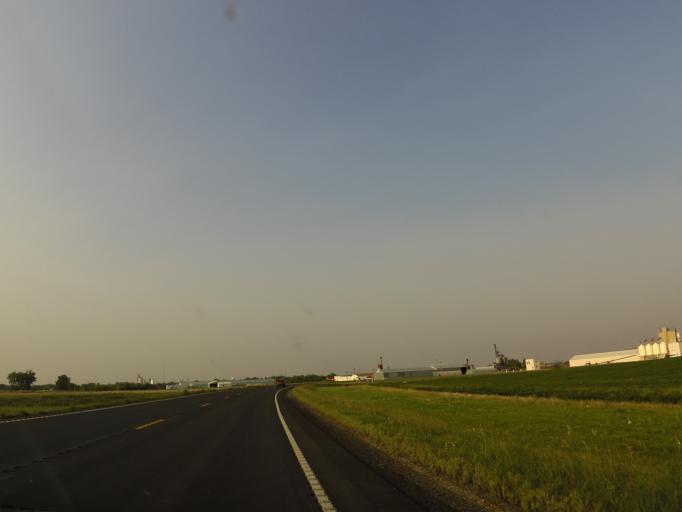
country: US
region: North Dakota
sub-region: Traill County
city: Mayville
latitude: 47.4791
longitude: -97.3254
